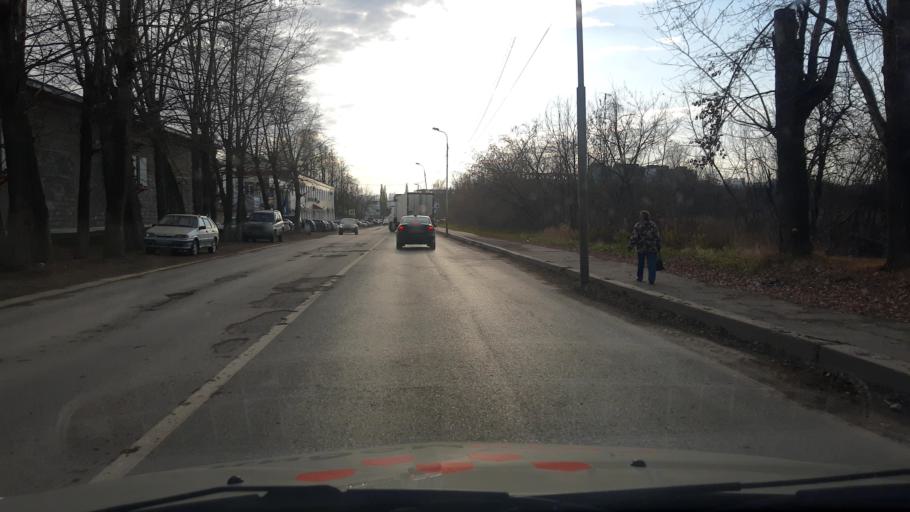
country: RU
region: Bashkortostan
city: Ufa
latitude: 54.8071
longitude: 56.0763
